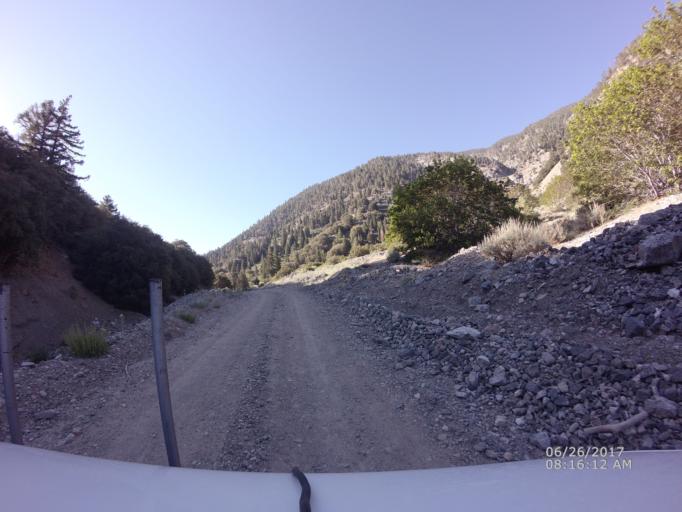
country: US
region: California
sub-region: San Bernardino County
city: Pinon Hills
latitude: 34.3795
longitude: -117.7649
